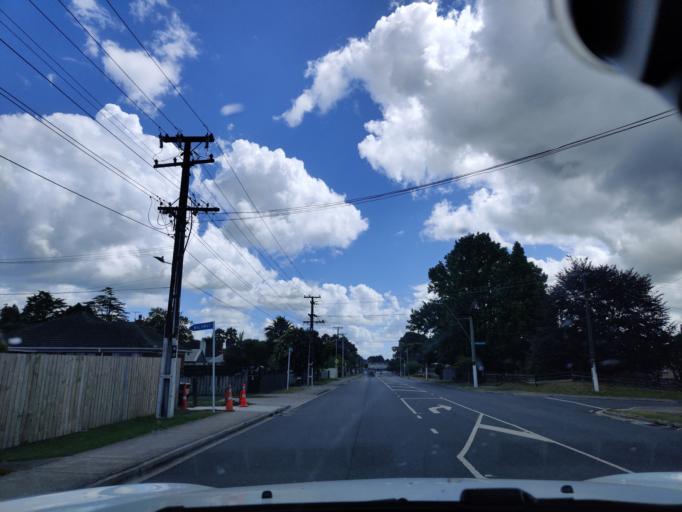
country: NZ
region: Auckland
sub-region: Auckland
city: Papakura
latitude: -37.0598
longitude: 174.9517
